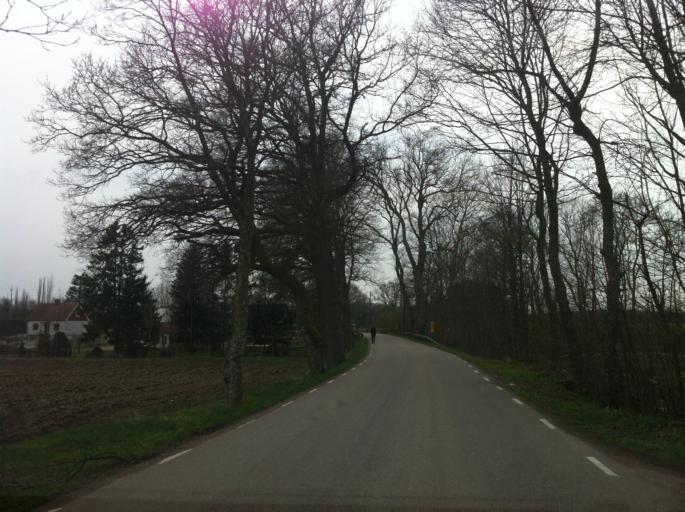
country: SE
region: Skane
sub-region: Klippans Kommun
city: Ljungbyhed
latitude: 55.9834
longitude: 13.1989
